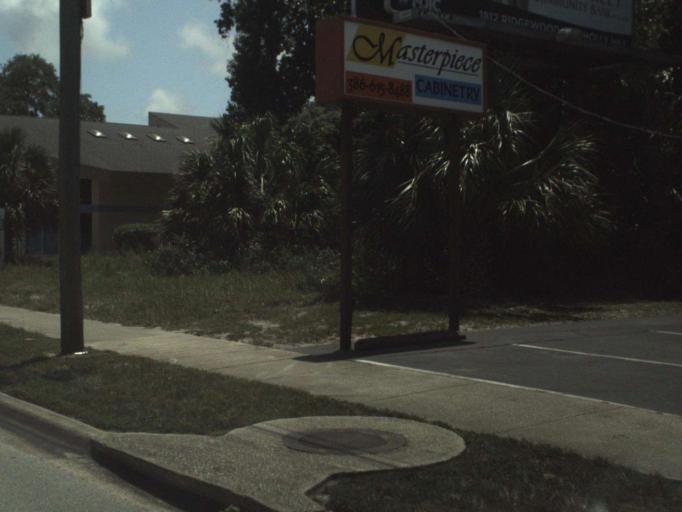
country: US
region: Florida
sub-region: Volusia County
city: Ormond Beach
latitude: 29.2657
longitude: -81.0525
